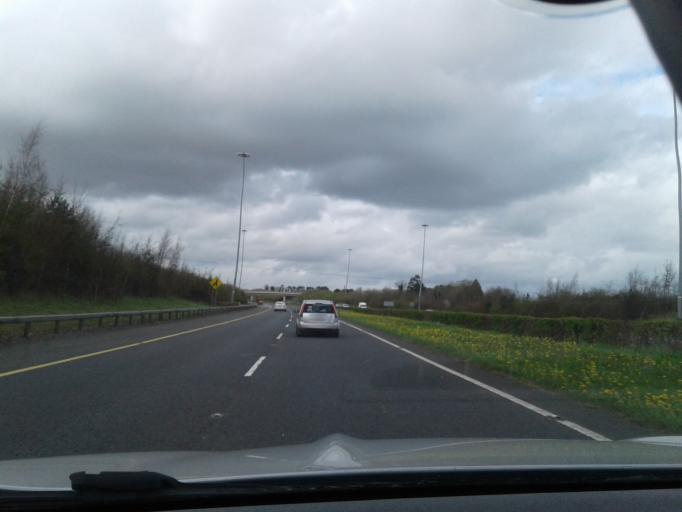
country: IE
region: Leinster
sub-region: Lu
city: Tullyallen
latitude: 53.7291
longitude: -6.3969
